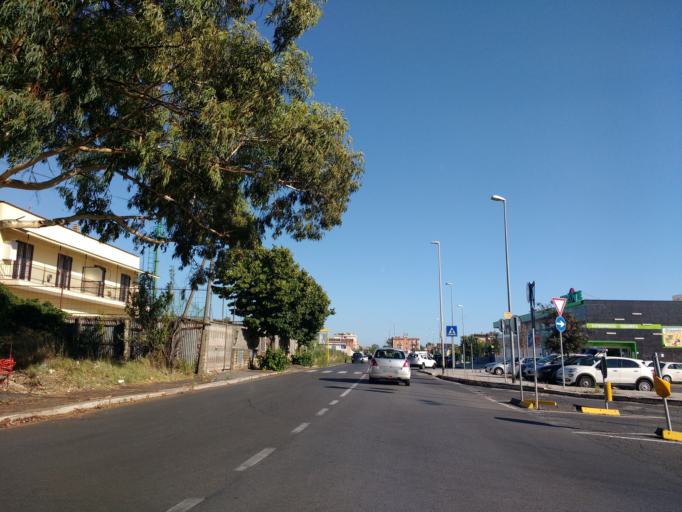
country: IT
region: Latium
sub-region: Citta metropolitana di Roma Capitale
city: Acilia-Castel Fusano-Ostia Antica
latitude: 41.7737
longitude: 12.3537
